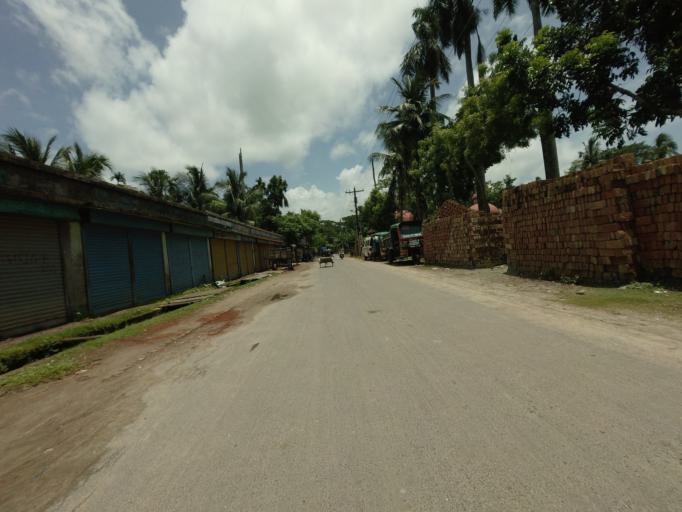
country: BD
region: Khulna
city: Kalia
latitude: 23.0369
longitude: 89.6327
